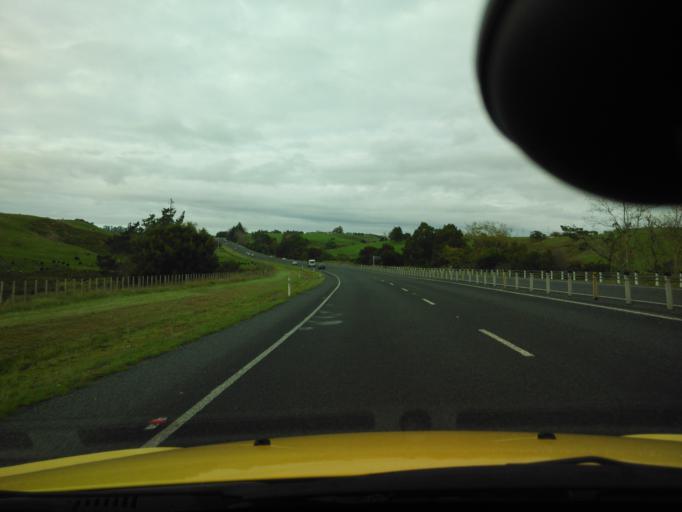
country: NZ
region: Waikato
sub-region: Waikato District
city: Te Kauwhata
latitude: -37.3723
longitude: 175.0938
